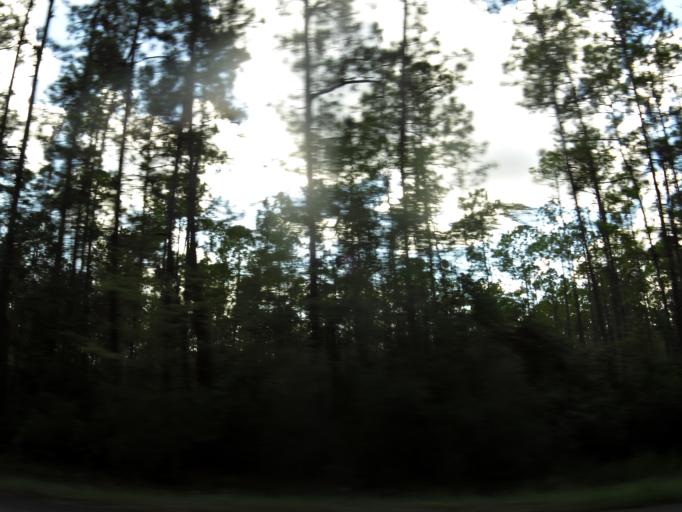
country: US
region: Georgia
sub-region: Echols County
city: Statenville
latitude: 30.7482
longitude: -83.1070
